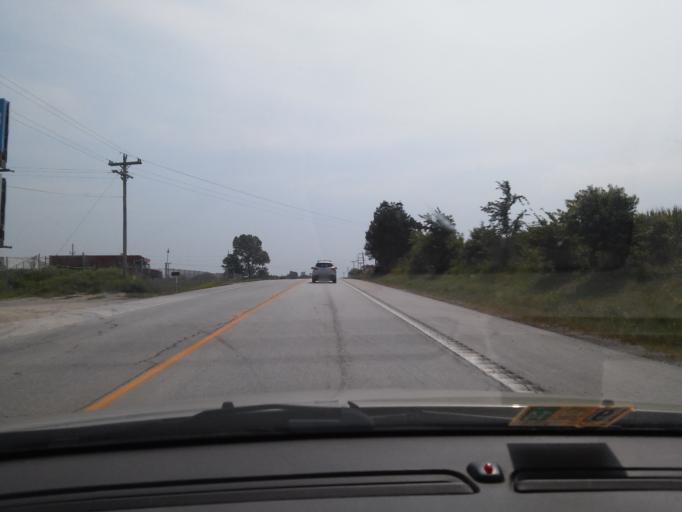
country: US
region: Missouri
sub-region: Audrain County
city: Mexico
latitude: 39.1638
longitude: -91.8051
